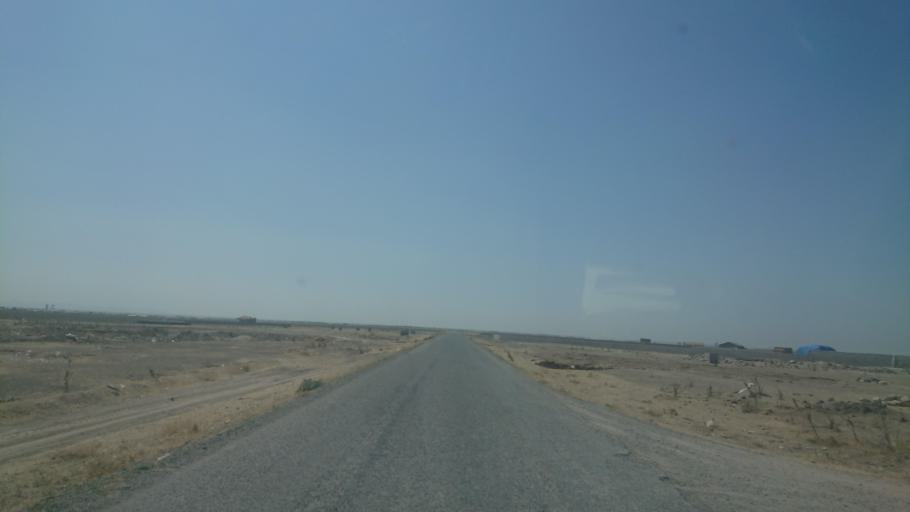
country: TR
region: Aksaray
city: Yesilova
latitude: 38.3292
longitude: 33.7484
